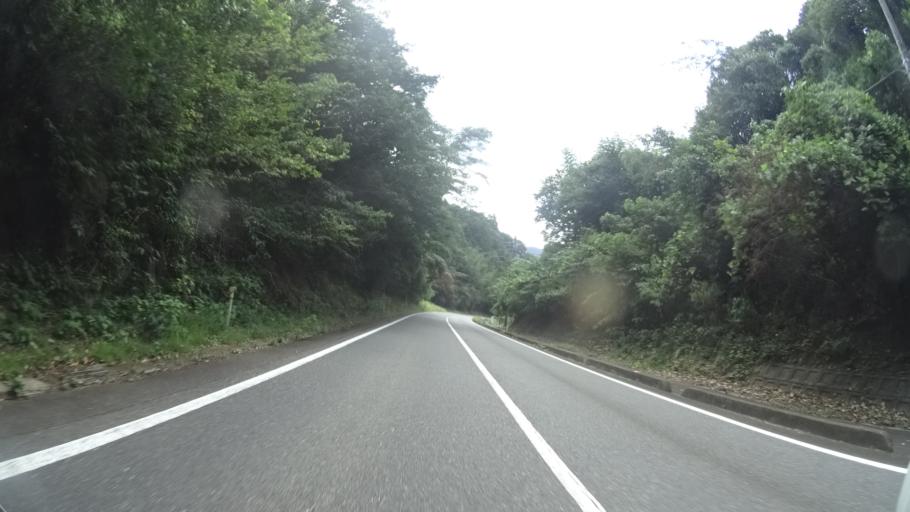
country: JP
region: Yamaguchi
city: Hagi
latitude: 34.4405
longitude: 131.4890
